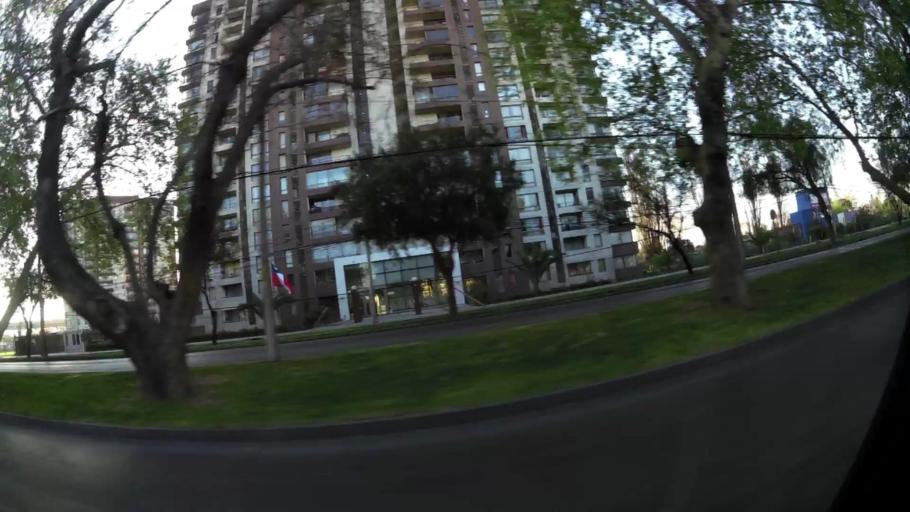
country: CL
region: Santiago Metropolitan
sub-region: Provincia de Santiago
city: Lo Prado
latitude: -33.4703
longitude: -70.7351
